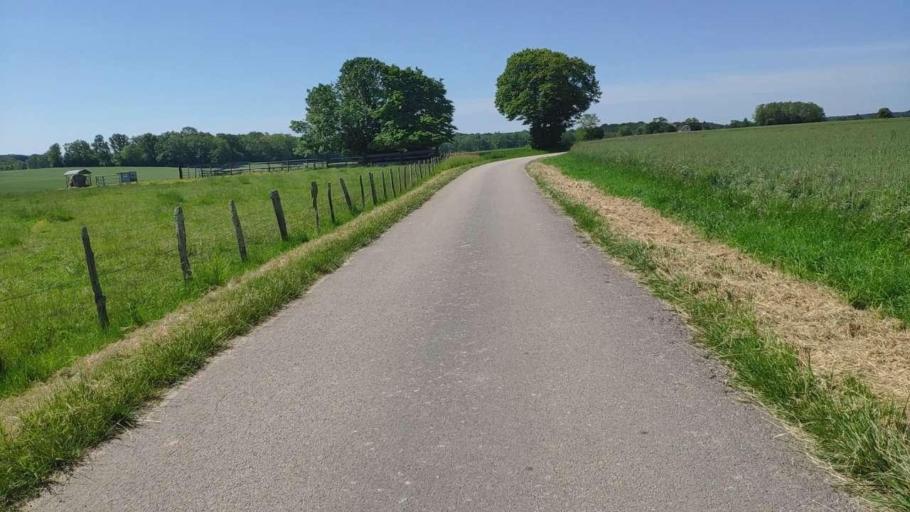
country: FR
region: Franche-Comte
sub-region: Departement du Jura
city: Bletterans
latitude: 46.7860
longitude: 5.4314
